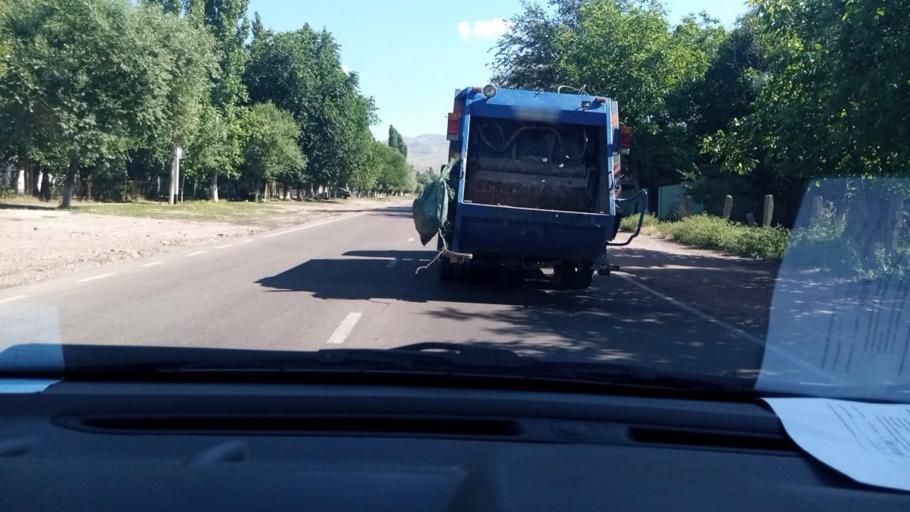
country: UZ
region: Toshkent
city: Angren
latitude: 41.0287
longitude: 70.0901
